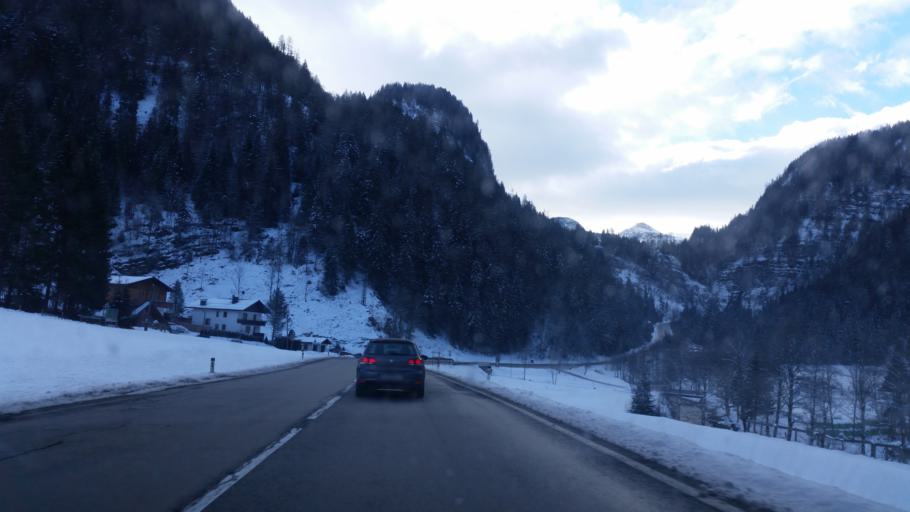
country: AT
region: Salzburg
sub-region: Politischer Bezirk Sankt Johann im Pongau
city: Untertauern
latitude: 47.3027
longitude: 13.5060
